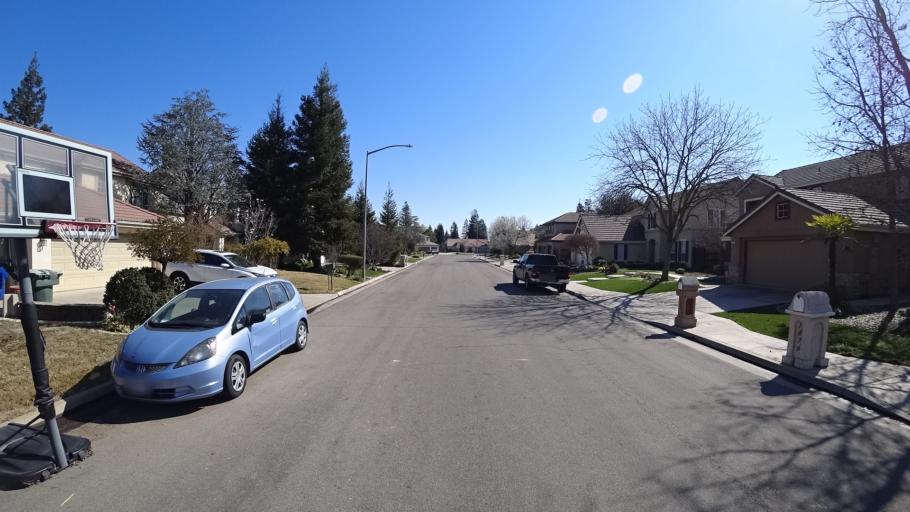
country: US
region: California
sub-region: Fresno County
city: Clovis
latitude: 36.8836
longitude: -119.7496
